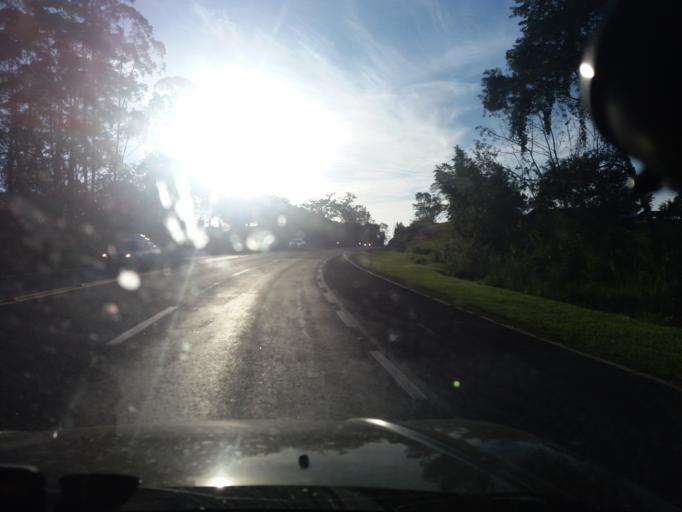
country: BR
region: Sao Paulo
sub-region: Buri
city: Buri
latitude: -23.9288
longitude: -48.6684
